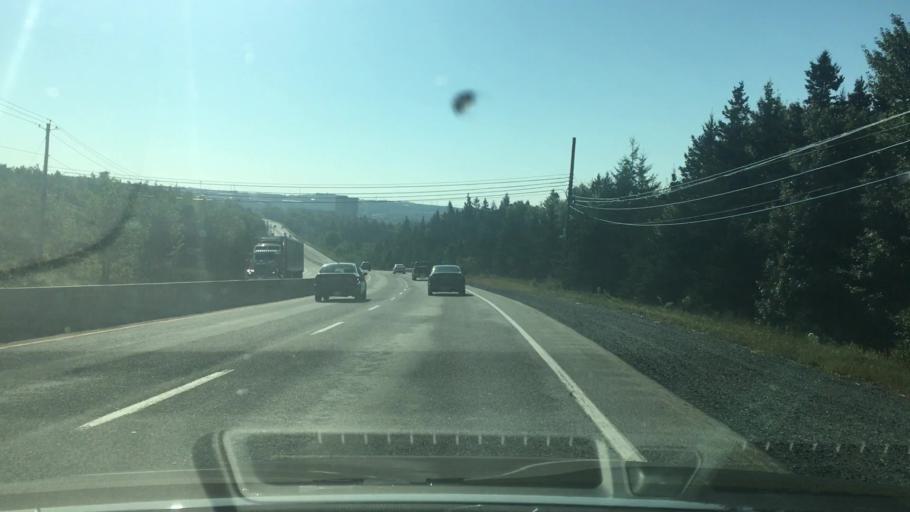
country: CA
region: Nova Scotia
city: Dartmouth
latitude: 44.7095
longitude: -63.6253
